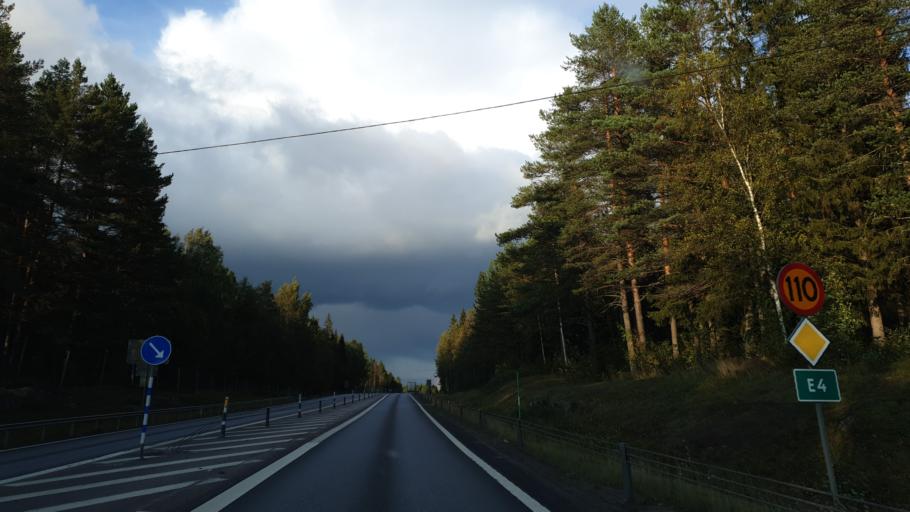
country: SE
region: Vaesterbotten
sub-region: Nordmalings Kommun
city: Nordmaling
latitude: 63.5122
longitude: 19.3586
